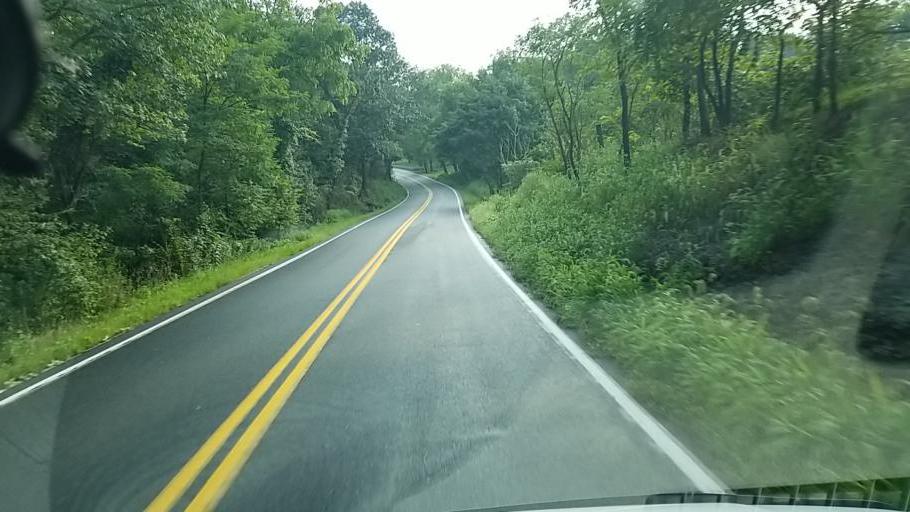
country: US
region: Pennsylvania
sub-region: Cumberland County
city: Newville
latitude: 40.1945
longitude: -77.4858
